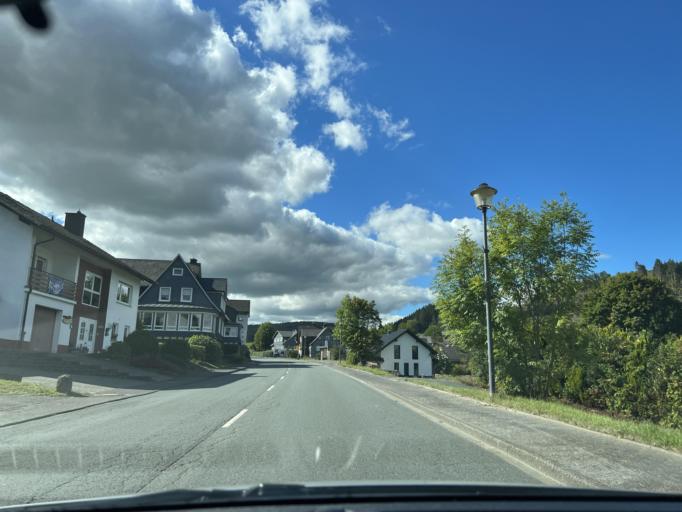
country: DE
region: North Rhine-Westphalia
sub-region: Regierungsbezirk Arnsberg
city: Bad Berleburg
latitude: 51.0151
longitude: 8.4144
